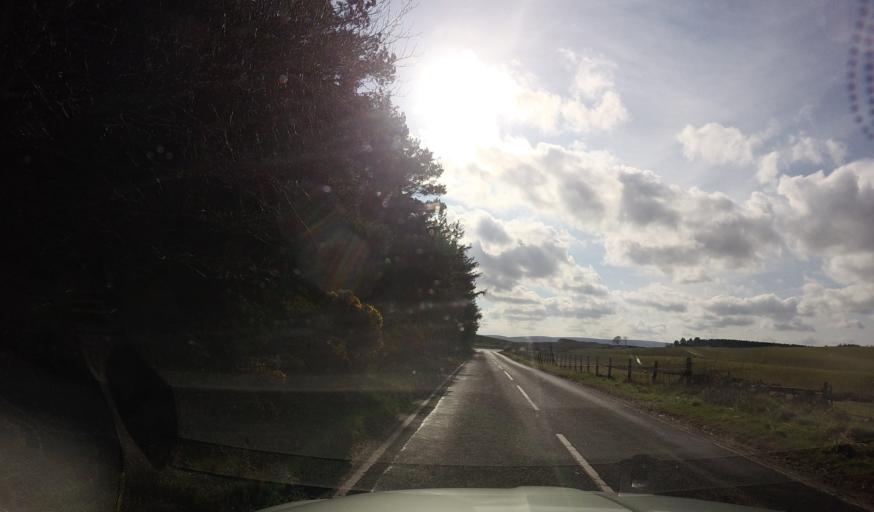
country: GB
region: Scotland
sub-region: Midlothian
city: Penicuik
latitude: 55.8121
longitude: -3.1878
